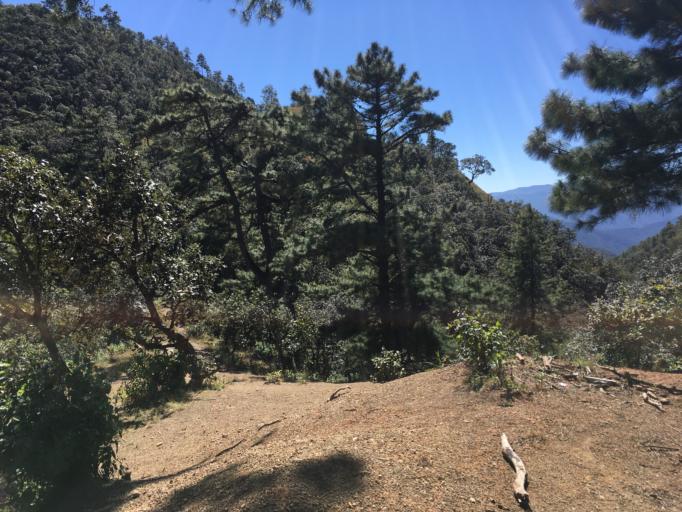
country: MM
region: Chin
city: Hakha
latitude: 22.2767
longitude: 93.6483
